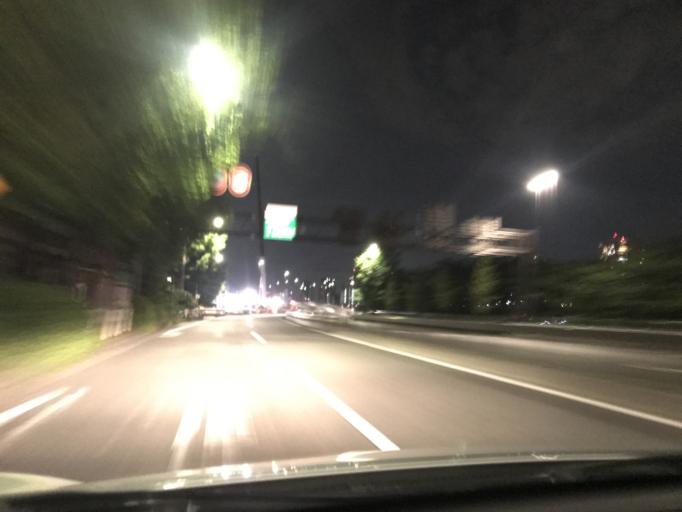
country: JP
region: Tokyo
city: Tokyo
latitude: 35.6212
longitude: 139.7537
